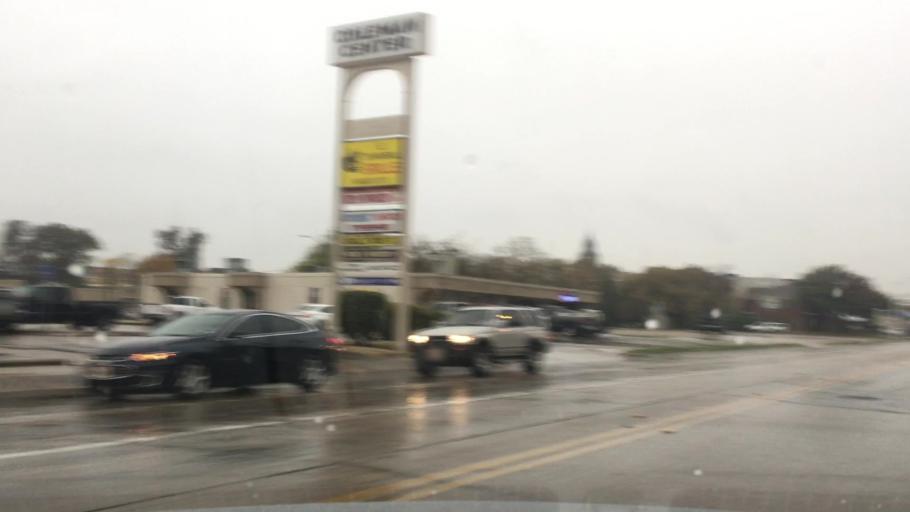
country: US
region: Texas
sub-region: Denton County
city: Denton
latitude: 33.2165
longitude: -97.1284
